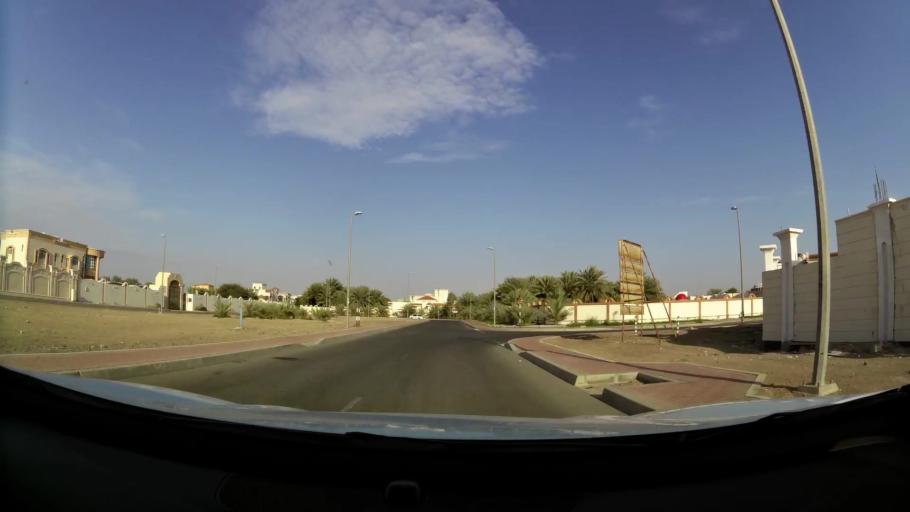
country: AE
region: Abu Dhabi
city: Al Ain
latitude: 24.0798
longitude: 55.8426
